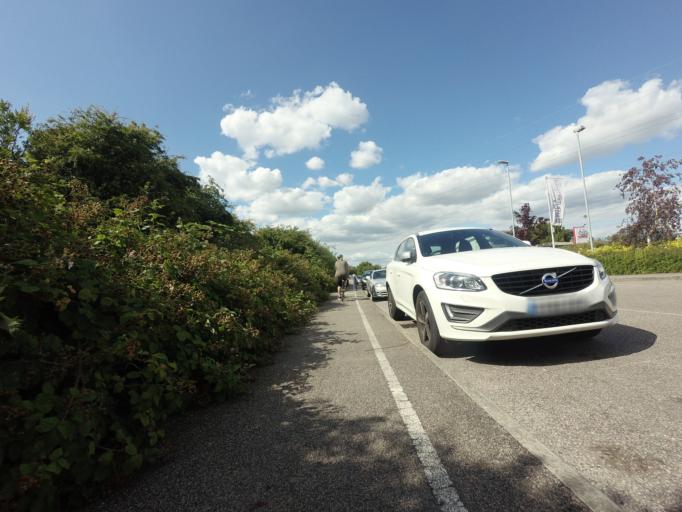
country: GB
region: England
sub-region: East Sussex
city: Eastbourne
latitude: 50.7989
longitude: 0.2891
